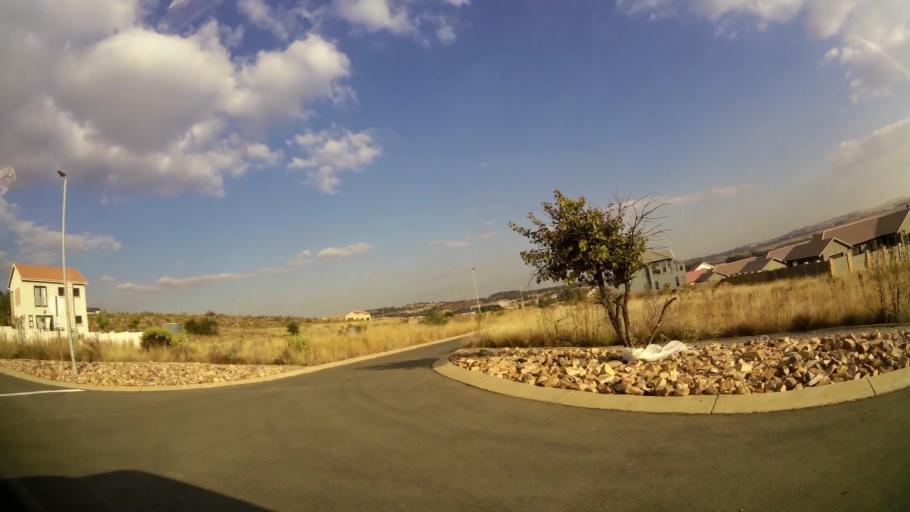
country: ZA
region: Gauteng
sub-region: West Rand District Municipality
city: Krugersdorp
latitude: -26.1019
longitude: 27.7298
